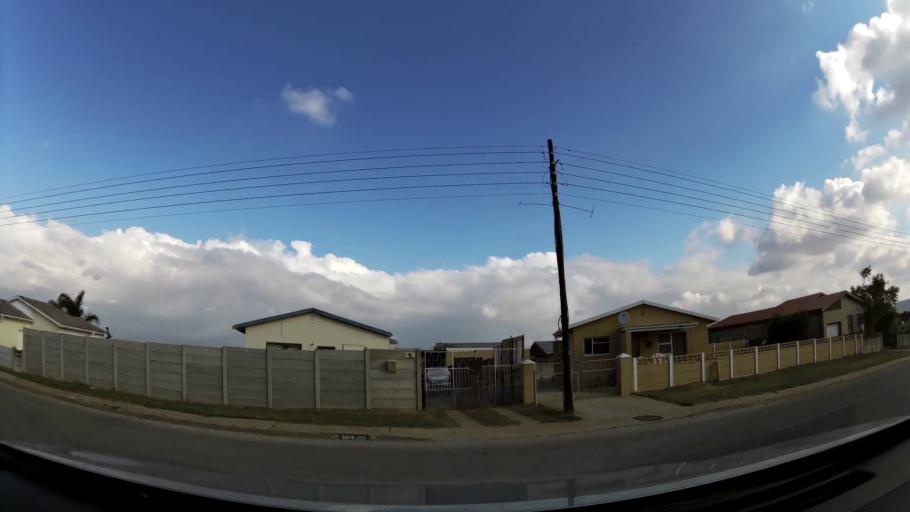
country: ZA
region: Eastern Cape
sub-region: Nelson Mandela Bay Metropolitan Municipality
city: Uitenhage
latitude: -33.7769
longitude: 25.4269
